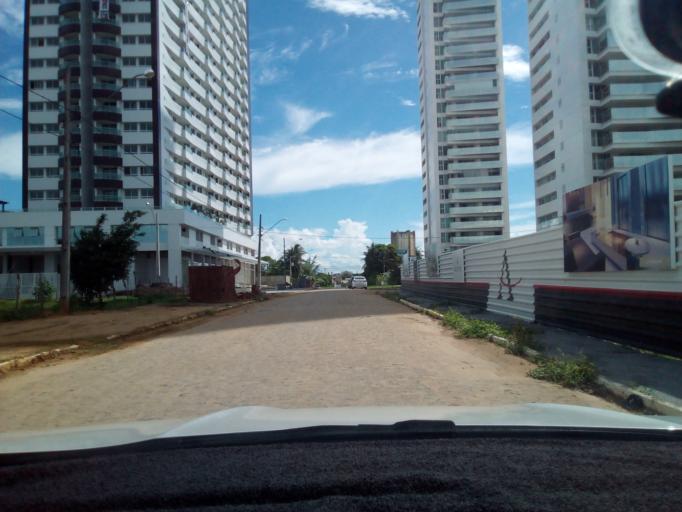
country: BR
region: Paraiba
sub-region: Joao Pessoa
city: Joao Pessoa
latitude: -7.1336
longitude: -34.8259
